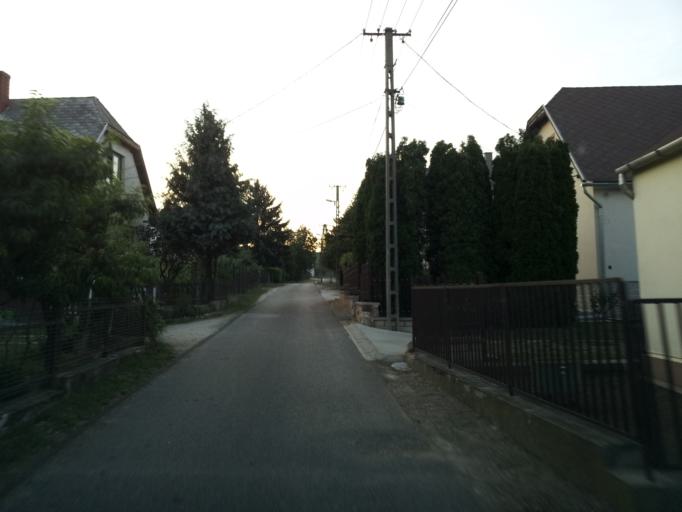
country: HU
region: Veszprem
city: Revfueloep
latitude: 46.9312
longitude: 17.5629
